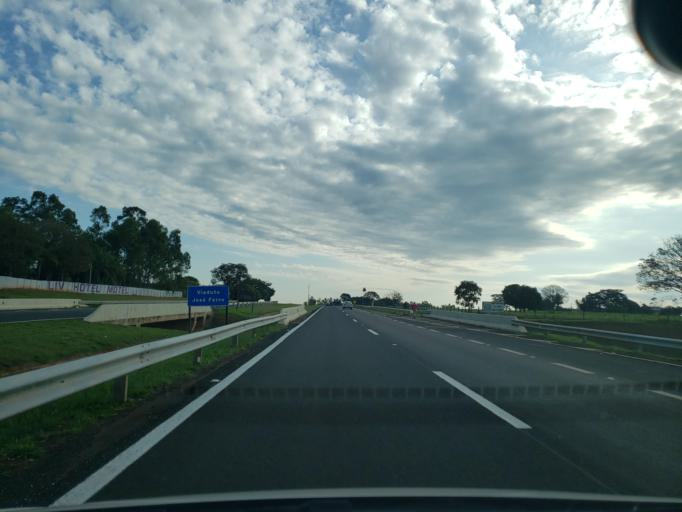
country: BR
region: Sao Paulo
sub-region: Guararapes
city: Guararapes
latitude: -21.2086
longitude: -50.6607
